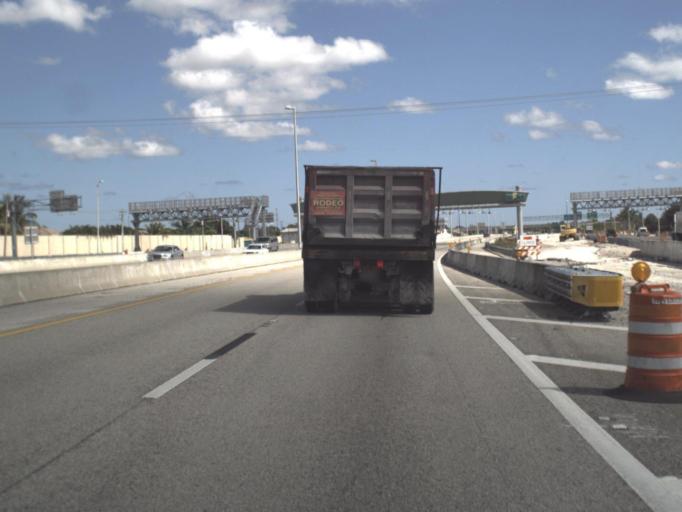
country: US
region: Florida
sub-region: Palm Beach County
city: Boca Pointe
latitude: 26.3050
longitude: -80.1778
